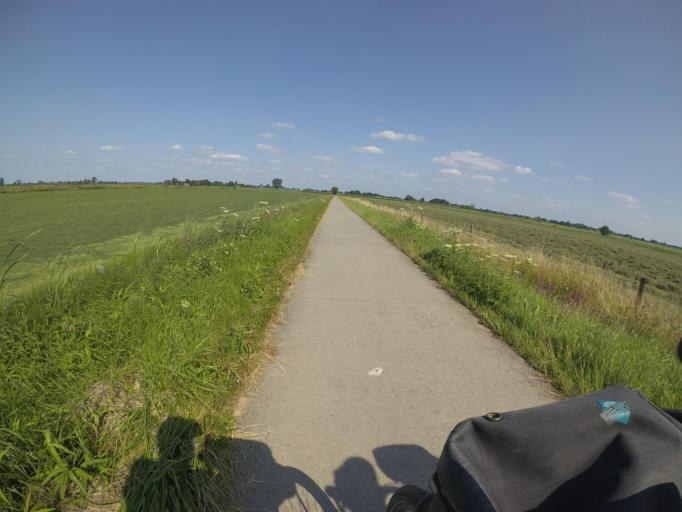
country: NL
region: Gelderland
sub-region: Gemeente Epe
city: Oene
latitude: 52.3425
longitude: 6.0667
